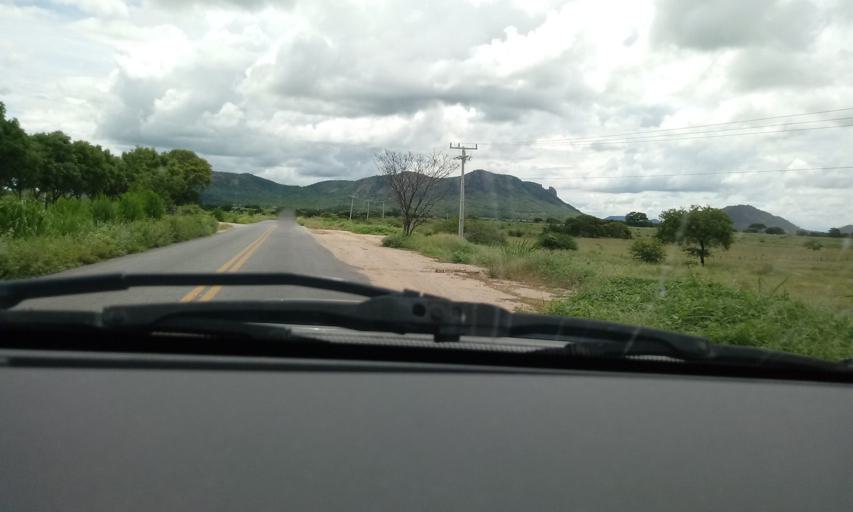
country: BR
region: Bahia
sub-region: Guanambi
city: Guanambi
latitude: -14.1617
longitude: -42.8164
